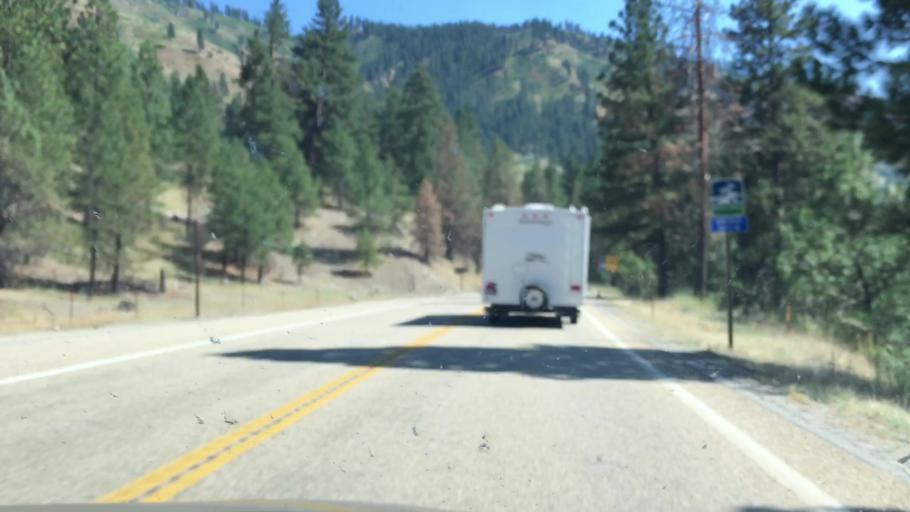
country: US
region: Idaho
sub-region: Boise County
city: Idaho City
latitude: 44.0764
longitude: -116.1207
